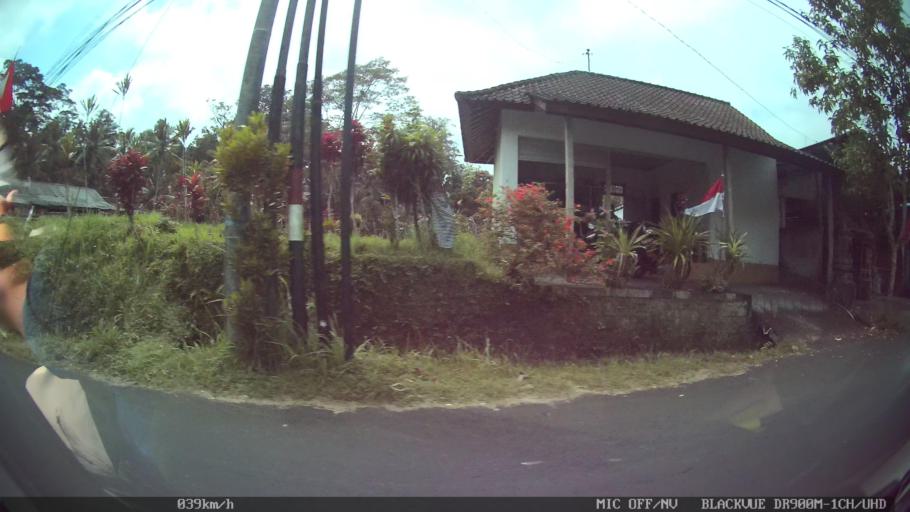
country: ID
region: Bali
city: Banjar Brahmanabukit
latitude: -8.4466
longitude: 115.3745
